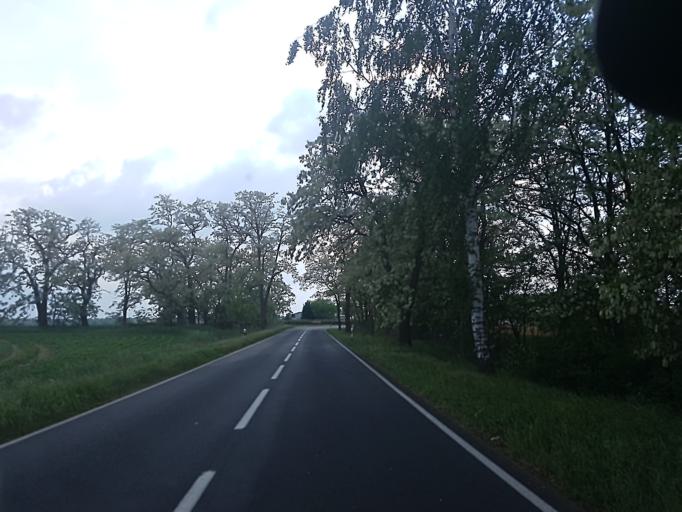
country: DE
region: Brandenburg
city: Gorzke
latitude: 52.0721
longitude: 12.3131
